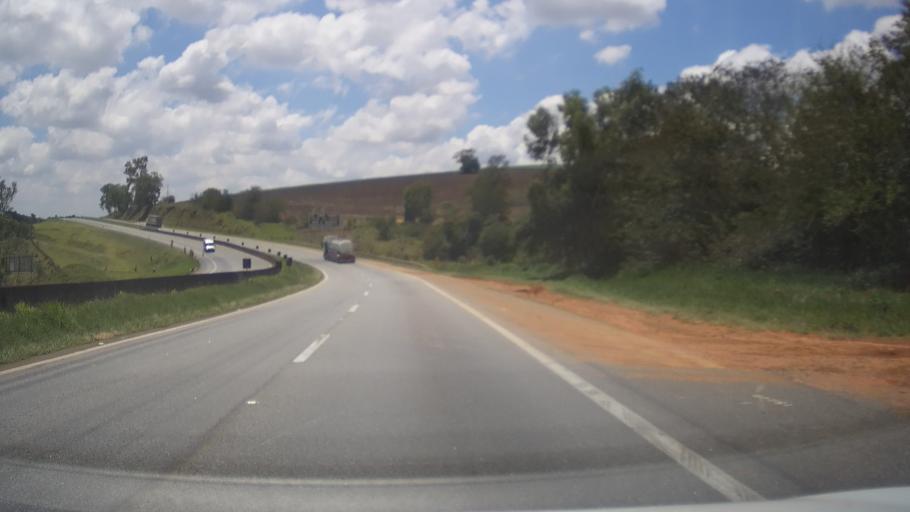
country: BR
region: Minas Gerais
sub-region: Campanha
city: Campanha
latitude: -21.8052
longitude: -45.4757
